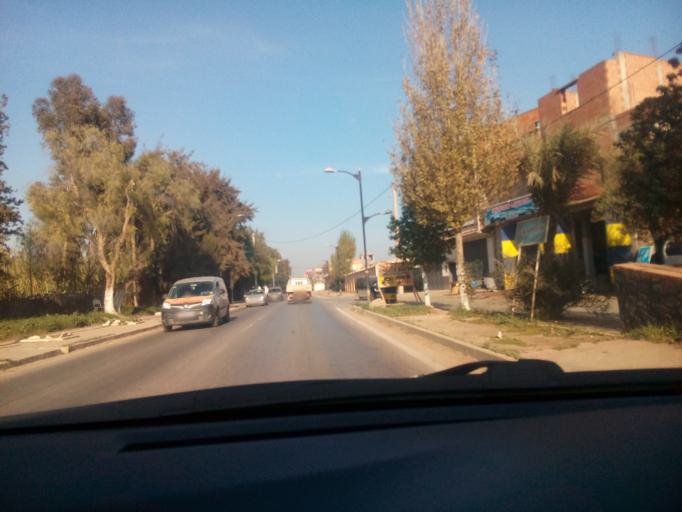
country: DZ
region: Oran
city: Es Senia
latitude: 35.6419
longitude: -0.6278
